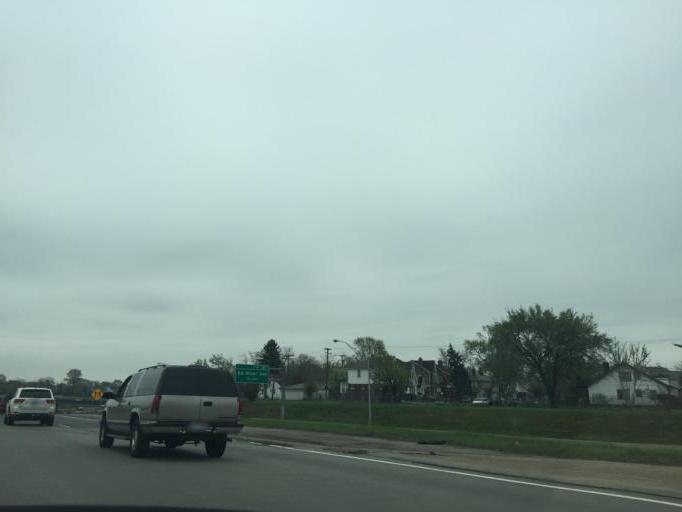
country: US
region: Michigan
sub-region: Wayne County
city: Highland Park
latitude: 42.3847
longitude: -83.1522
